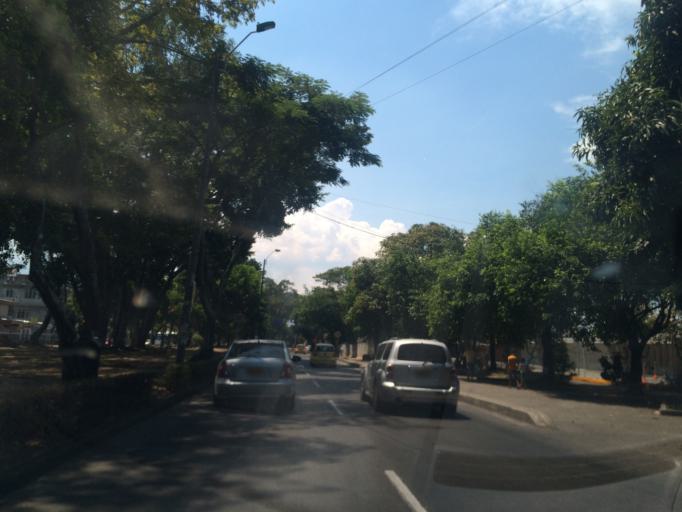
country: CO
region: Valle del Cauca
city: Cali
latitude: 3.4664
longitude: -76.5015
